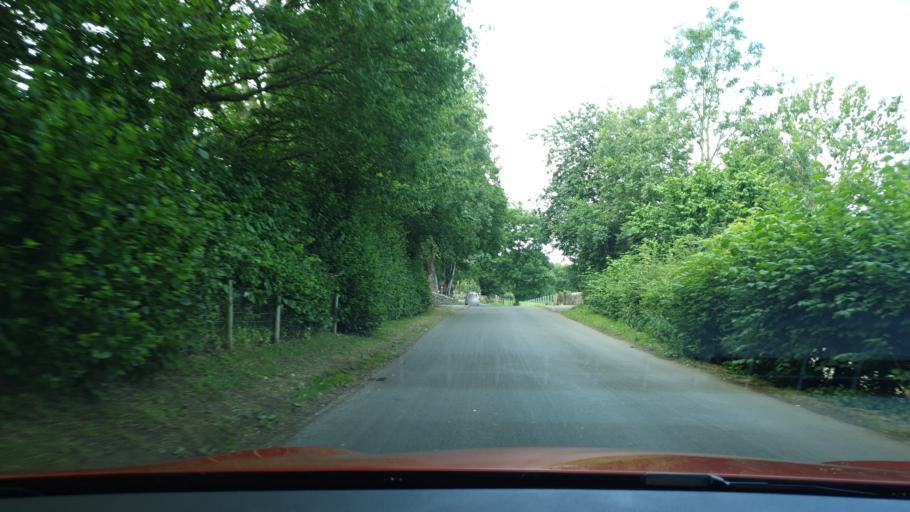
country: GB
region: England
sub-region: Cumbria
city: Penrith
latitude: 54.6048
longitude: -2.8230
